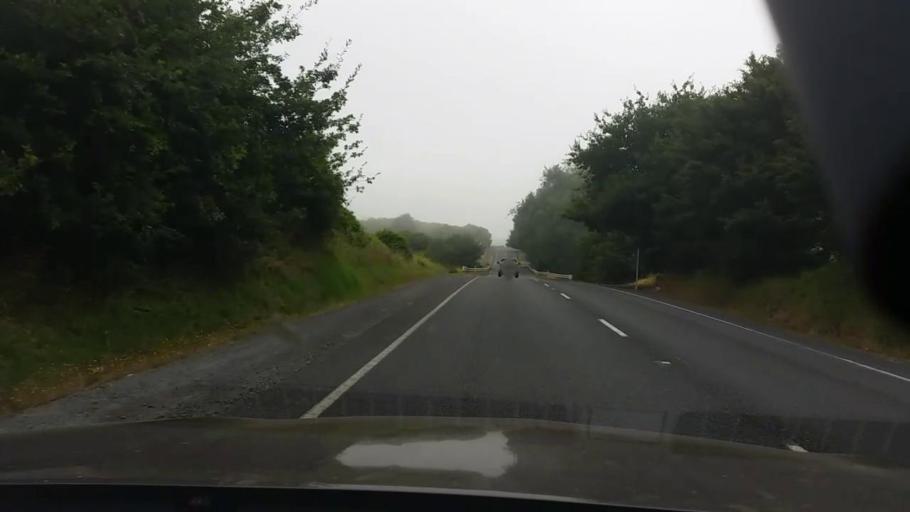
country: NZ
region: Waikato
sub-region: Hamilton City
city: Hamilton
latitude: -37.6547
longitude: 175.2928
